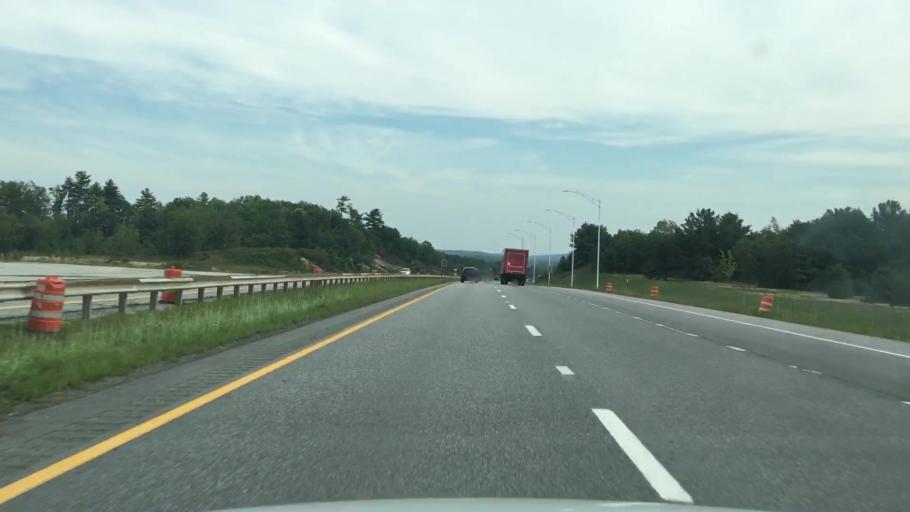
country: US
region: Maine
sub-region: Cumberland County
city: Cumberland Center
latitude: 43.8138
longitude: -70.3179
